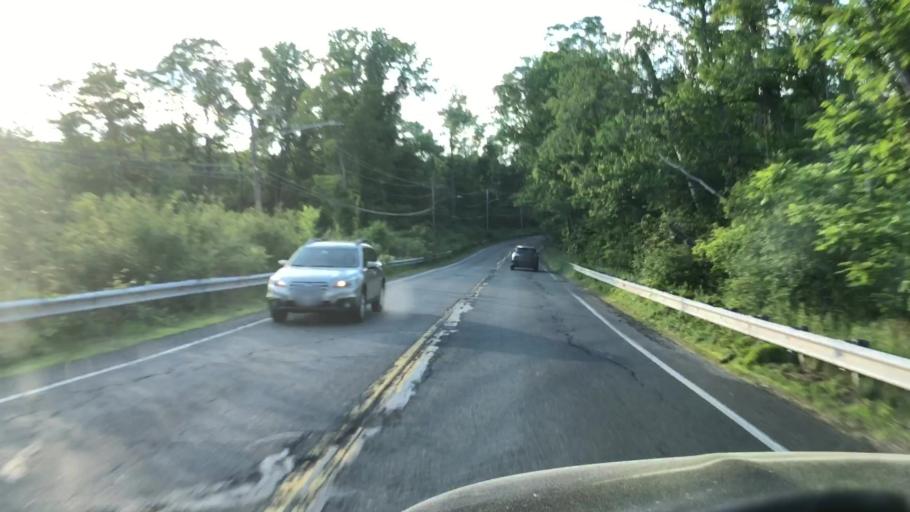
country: US
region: Massachusetts
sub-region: Hampshire County
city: Easthampton
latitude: 42.2313
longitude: -72.6484
